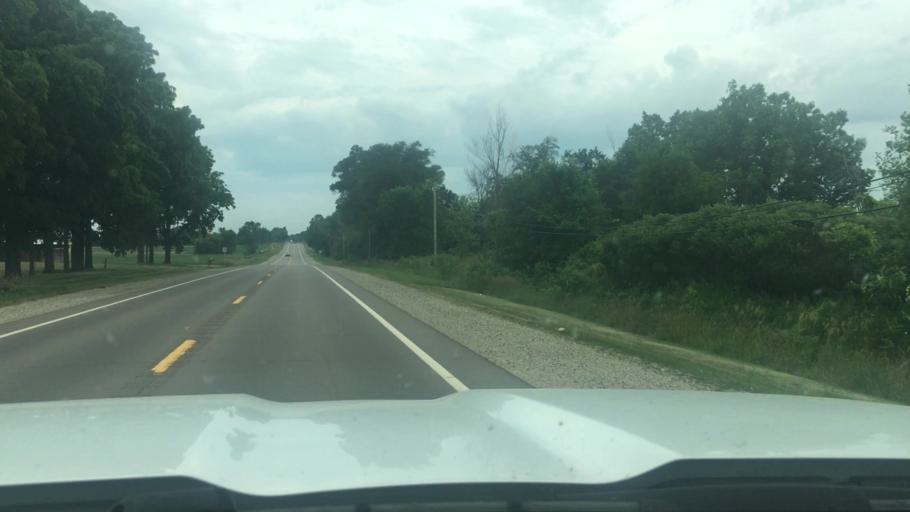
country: US
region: Michigan
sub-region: Clinton County
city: Fowler
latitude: 43.0019
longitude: -84.8049
